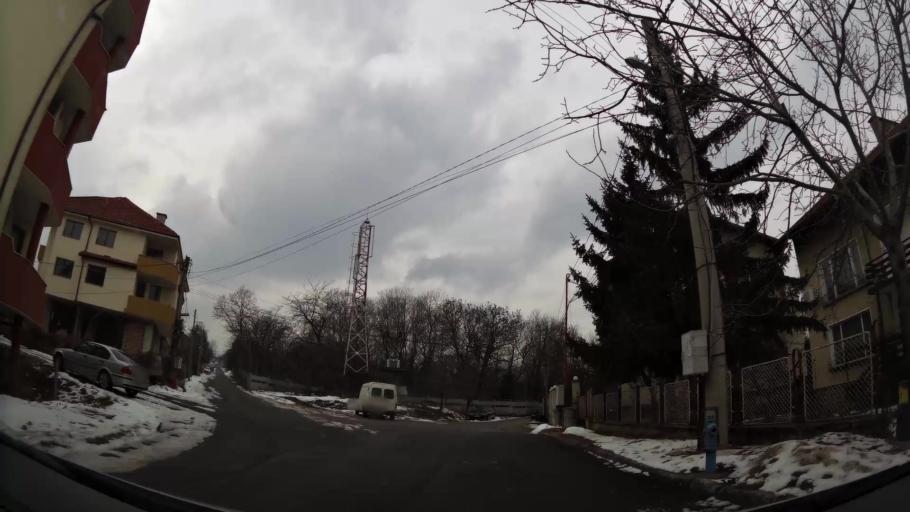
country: BG
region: Sofiya
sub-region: Obshtina Bozhurishte
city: Bozhurishte
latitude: 42.6780
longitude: 23.2337
